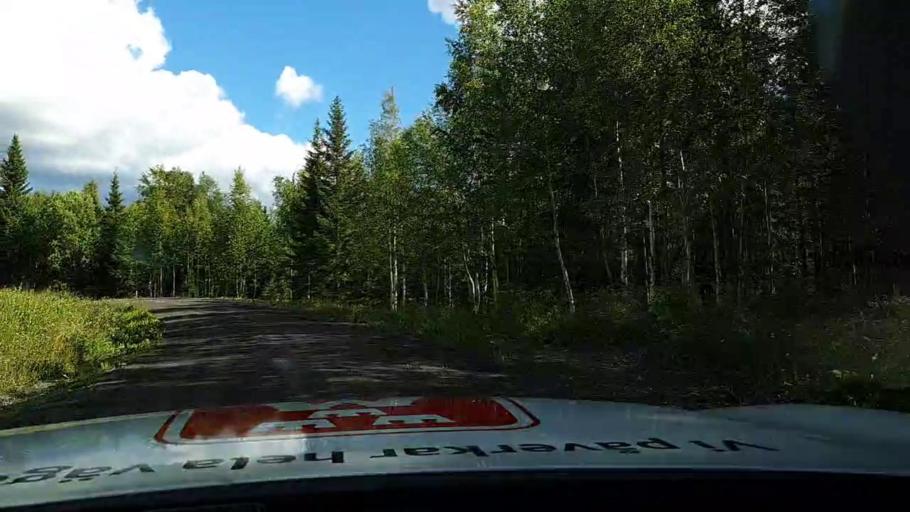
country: SE
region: Jaemtland
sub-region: Krokoms Kommun
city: Valla
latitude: 63.3201
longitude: 13.7597
